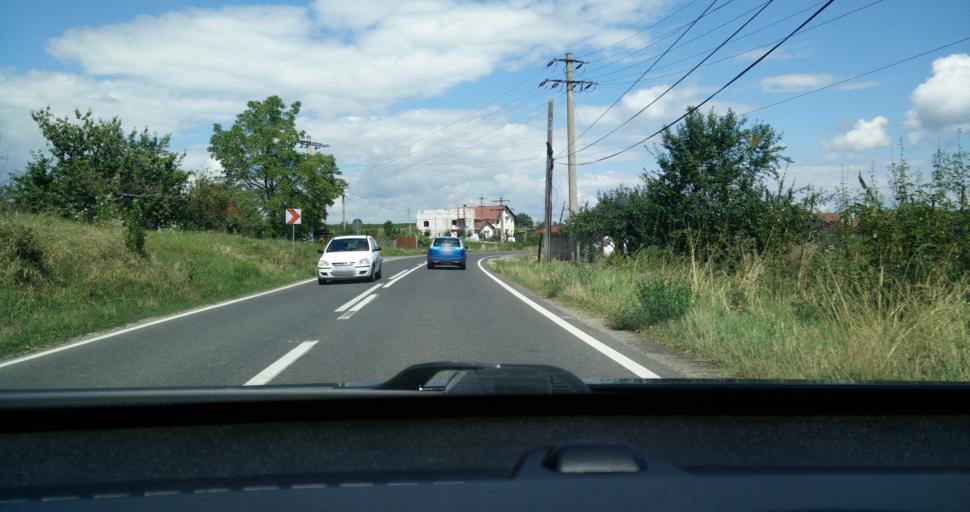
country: RO
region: Alba
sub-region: Municipiul Sebes
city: Petresti
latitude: 45.9104
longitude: 23.5542
